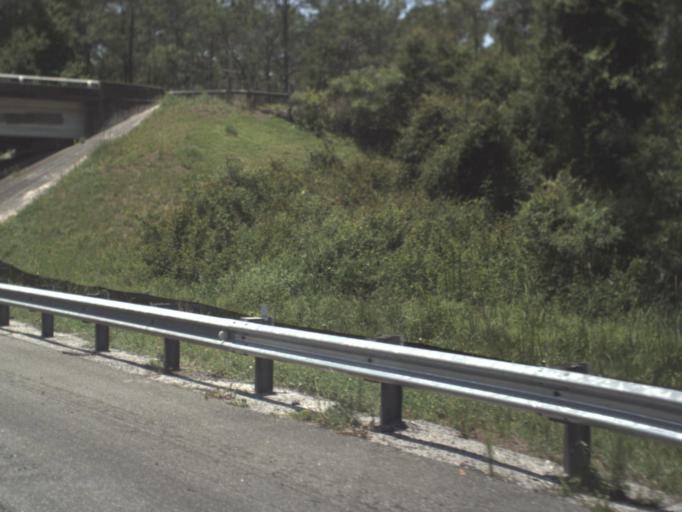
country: US
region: Florida
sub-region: Columbia County
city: Watertown
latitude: 30.2439
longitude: -82.5701
